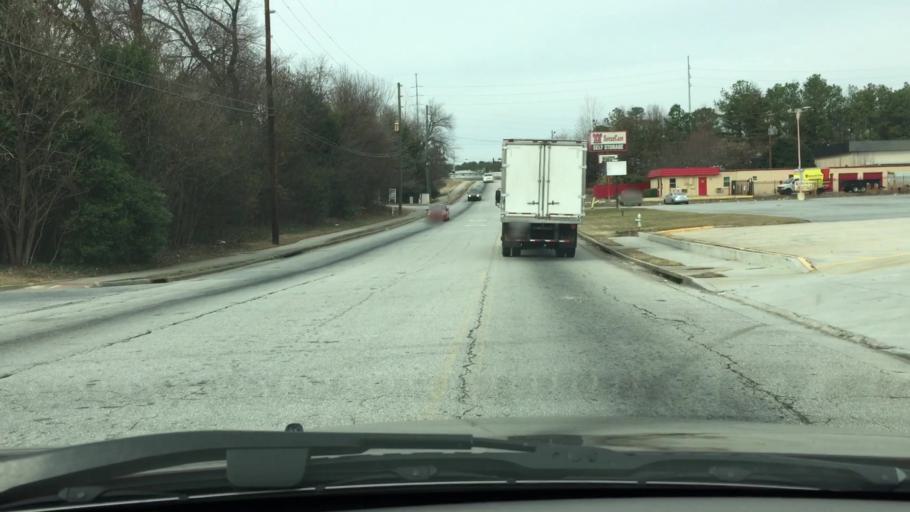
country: US
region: Georgia
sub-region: DeKalb County
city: Doraville
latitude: 33.9058
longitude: -84.2716
